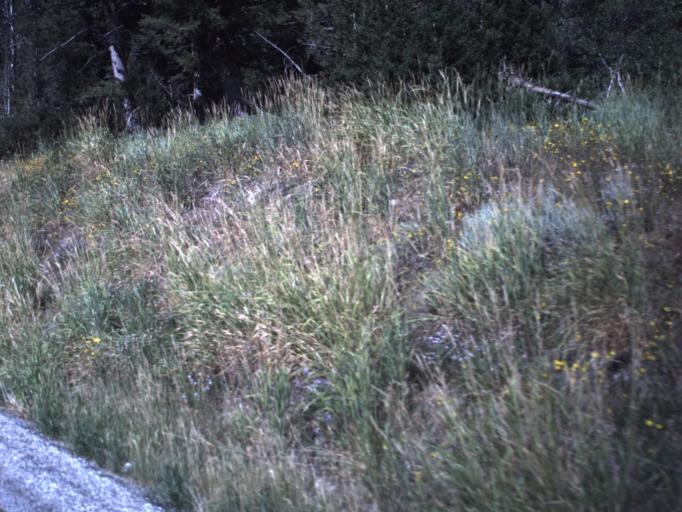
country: US
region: Utah
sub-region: Cache County
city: Richmond
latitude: 41.9477
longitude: -111.5459
